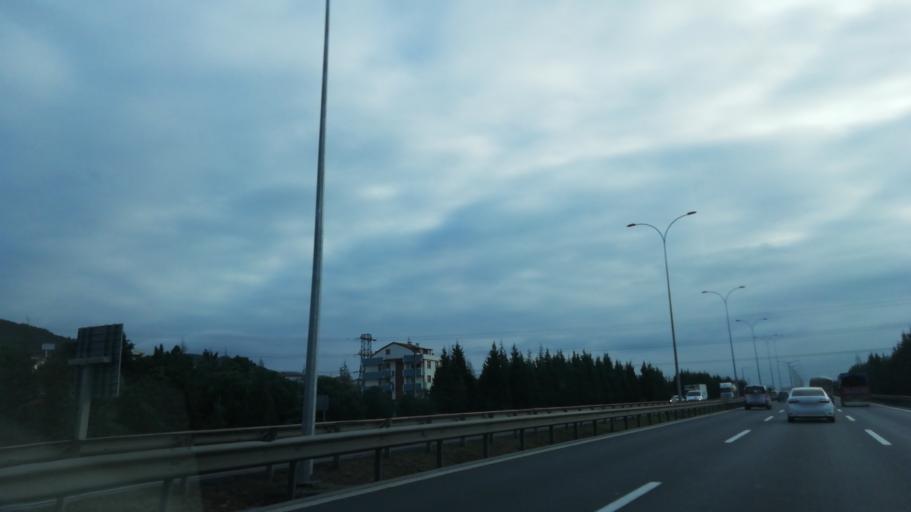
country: TR
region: Kocaeli
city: Korfez
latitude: 40.7731
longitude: 29.7667
